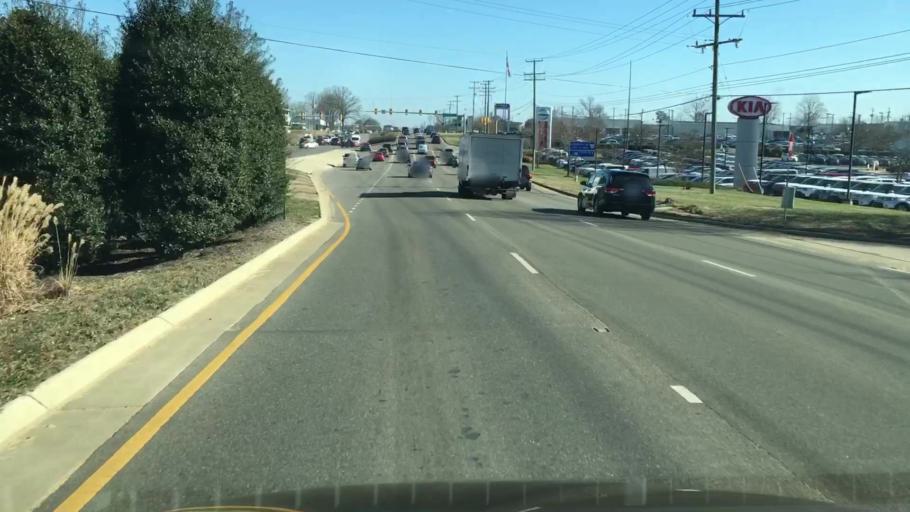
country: US
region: Virginia
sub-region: Chesterfield County
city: Bon Air
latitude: 37.5044
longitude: -77.6199
